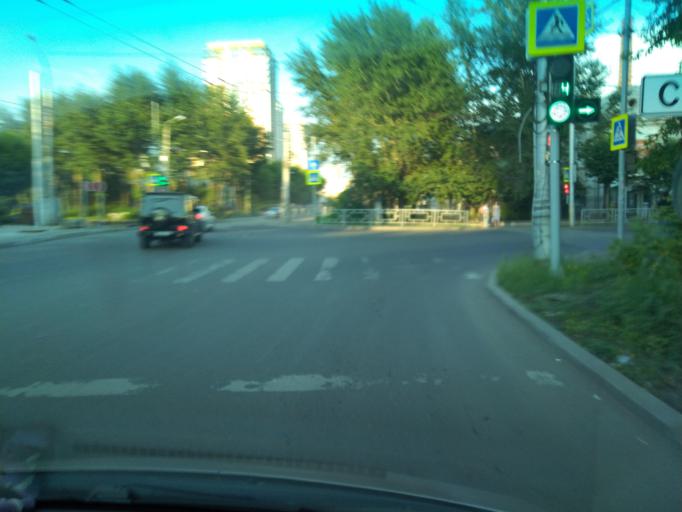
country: RU
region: Krasnoyarskiy
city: Krasnoyarsk
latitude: 56.0313
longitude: 92.9071
